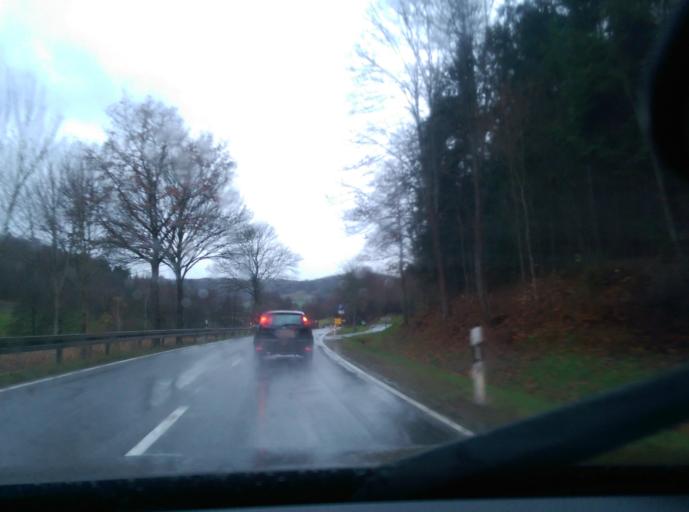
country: DE
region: Thuringia
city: Gerstungen
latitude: 51.0260
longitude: 10.0174
